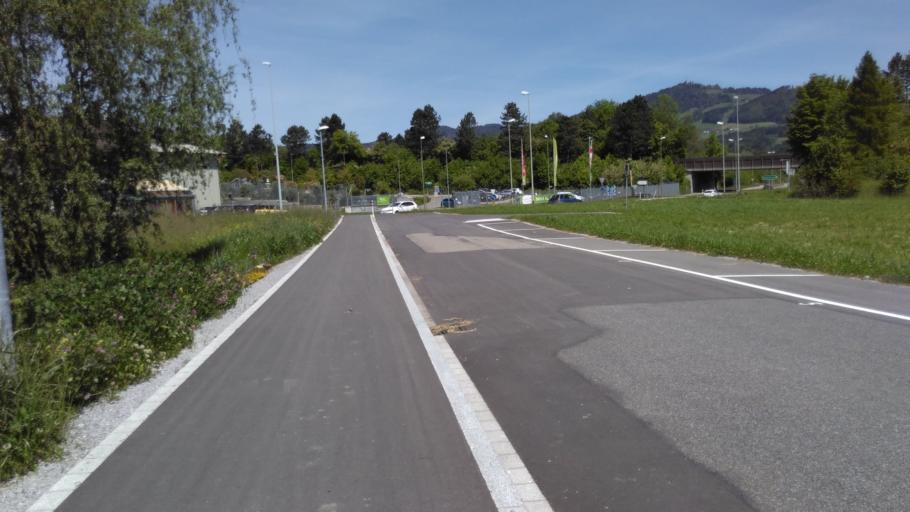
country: CH
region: Zurich
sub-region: Bezirk Hinwil
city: Bubikon
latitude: 47.2735
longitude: 8.8279
